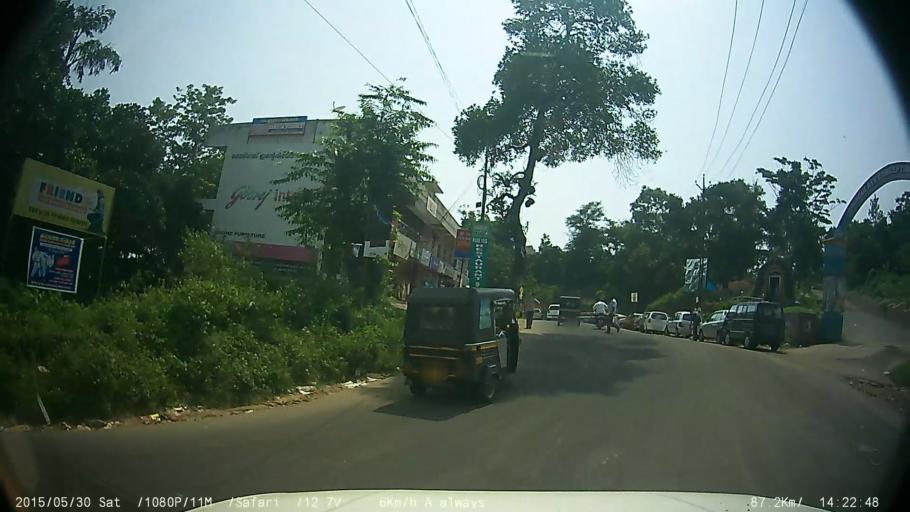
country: IN
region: Kerala
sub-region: Wayanad
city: Panamaram
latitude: 11.8007
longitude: 76.0054
